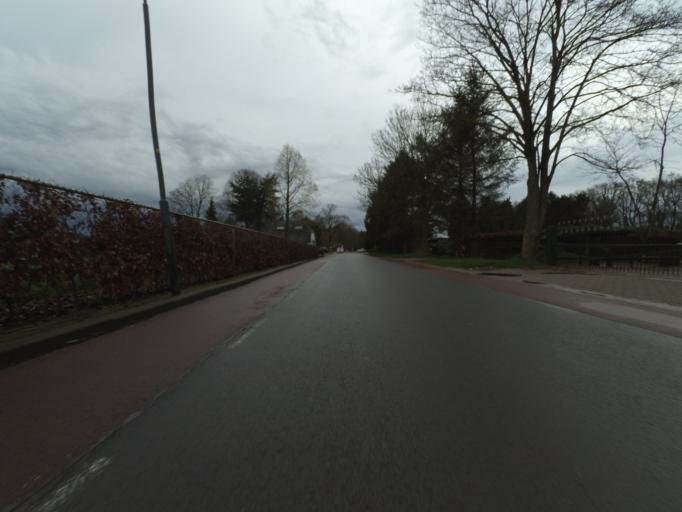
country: NL
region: Gelderland
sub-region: Gemeente Apeldoorn
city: Beekbergen
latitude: 52.1612
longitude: 5.9542
